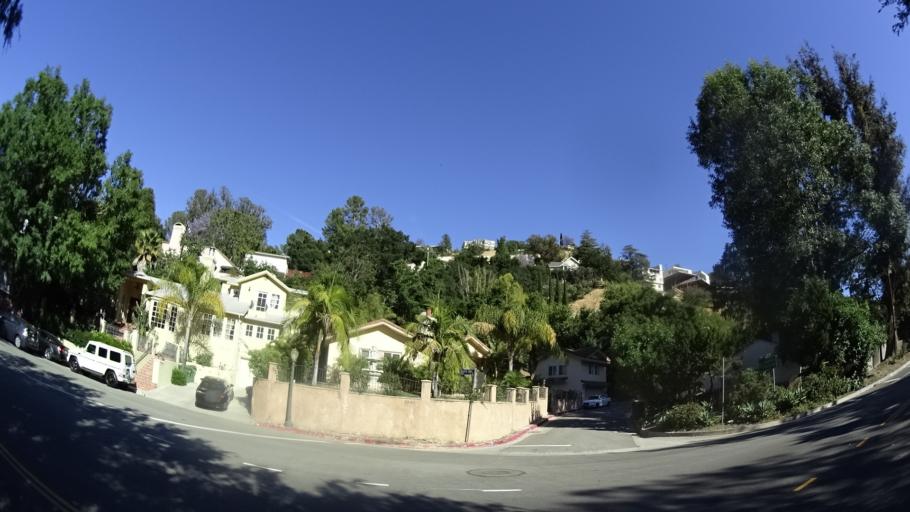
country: US
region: California
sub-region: Los Angeles County
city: Sherman Oaks
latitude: 34.1427
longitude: -118.4483
